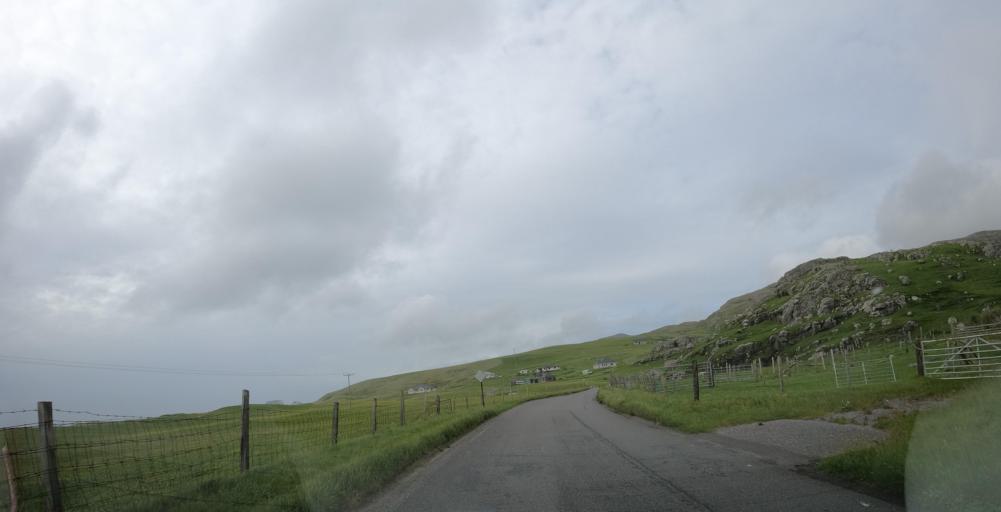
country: GB
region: Scotland
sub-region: Eilean Siar
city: Barra
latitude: 56.9711
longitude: -7.5162
